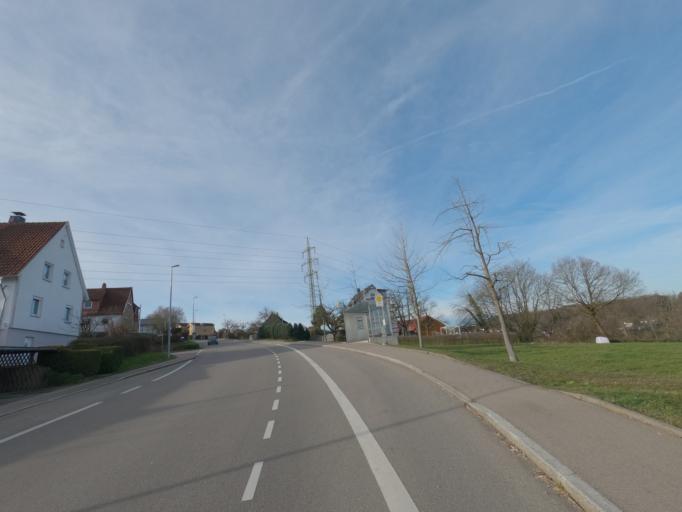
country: DE
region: Baden-Wuerttemberg
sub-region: Regierungsbezirk Stuttgart
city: Uhingen
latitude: 48.7016
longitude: 9.5790
